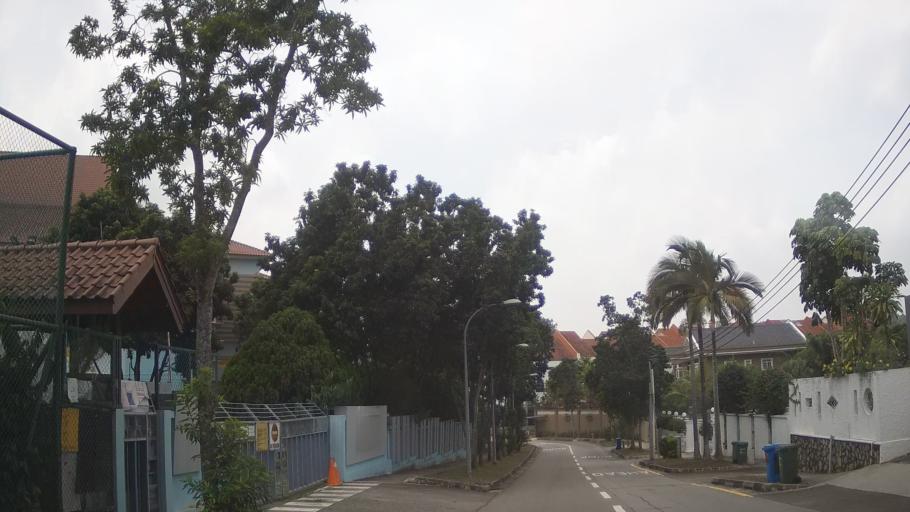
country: MY
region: Johor
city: Johor Bahru
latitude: 1.3699
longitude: 103.7703
